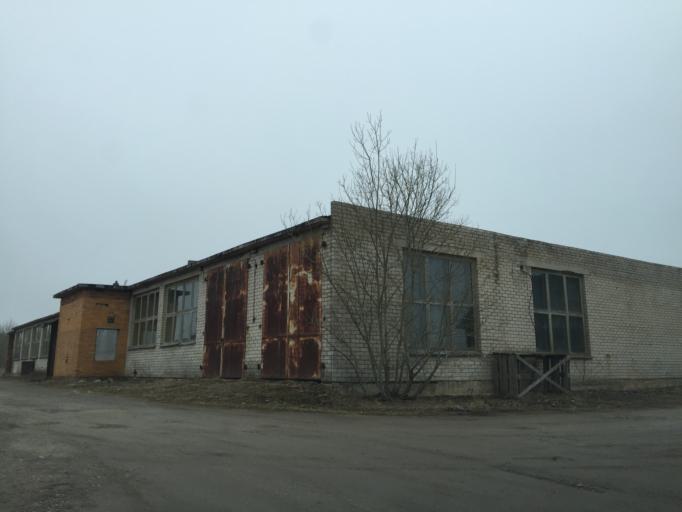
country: EE
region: Laeaene
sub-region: Lihula vald
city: Lihula
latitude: 58.5879
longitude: 23.5249
